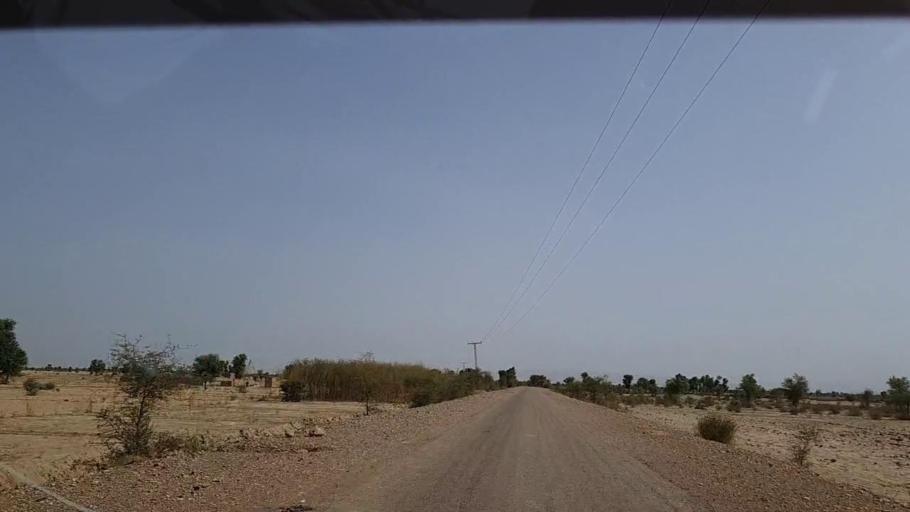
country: PK
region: Sindh
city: Johi
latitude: 26.6578
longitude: 67.5058
